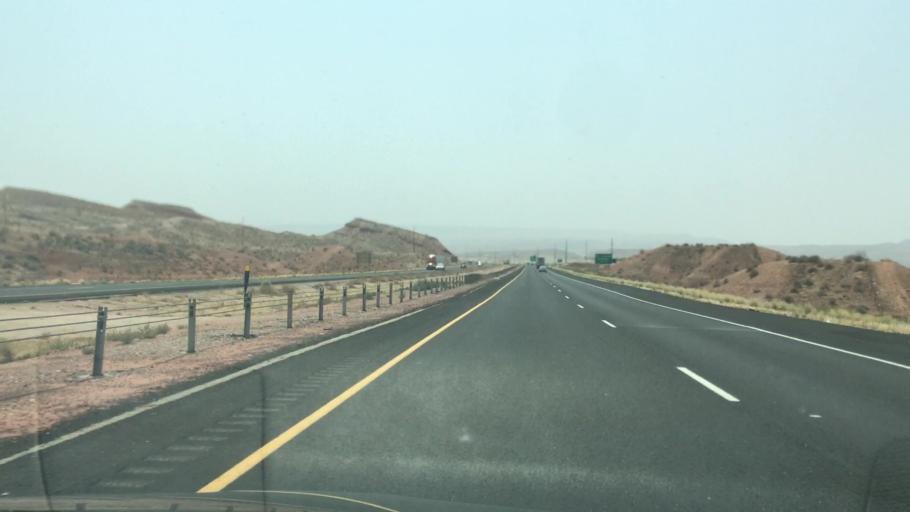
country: US
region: Utah
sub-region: Washington County
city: Saint George
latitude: 37.0433
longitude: -113.5932
